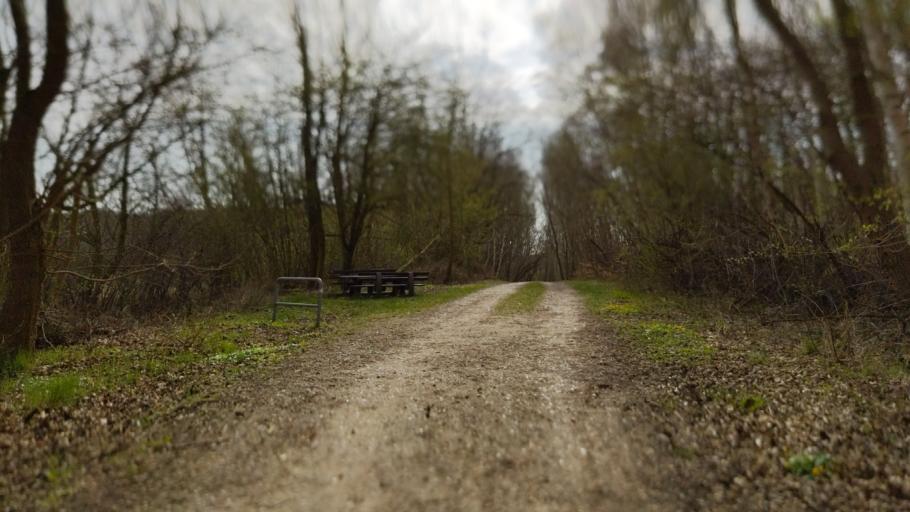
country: DE
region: Schleswig-Holstein
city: Travemuende
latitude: 53.9632
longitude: 10.9314
